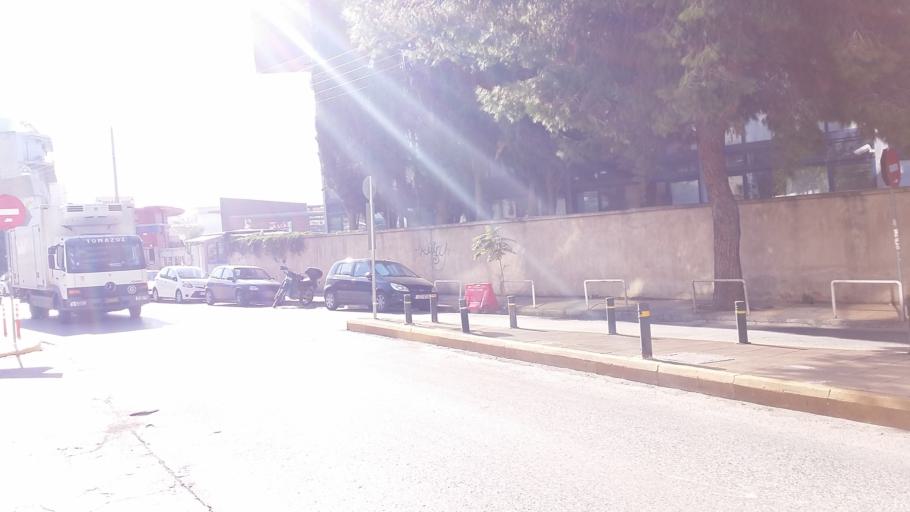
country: GR
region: Attica
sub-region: Nomarchia Athinas
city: Nea Ionia
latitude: 38.0425
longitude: 23.7610
